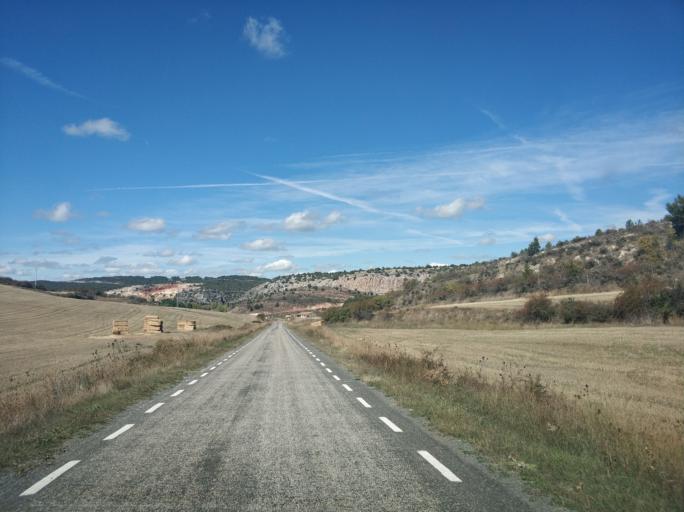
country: ES
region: Castille and Leon
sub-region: Provincia de Soria
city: Espejon
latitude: 41.8269
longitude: -3.2509
